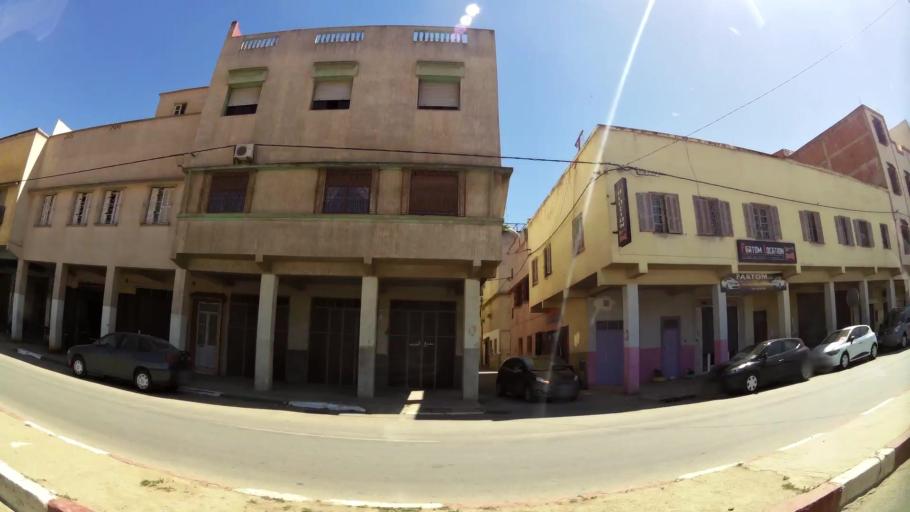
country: MA
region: Meknes-Tafilalet
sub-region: Meknes
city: Meknes
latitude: 33.8700
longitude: -5.5531
